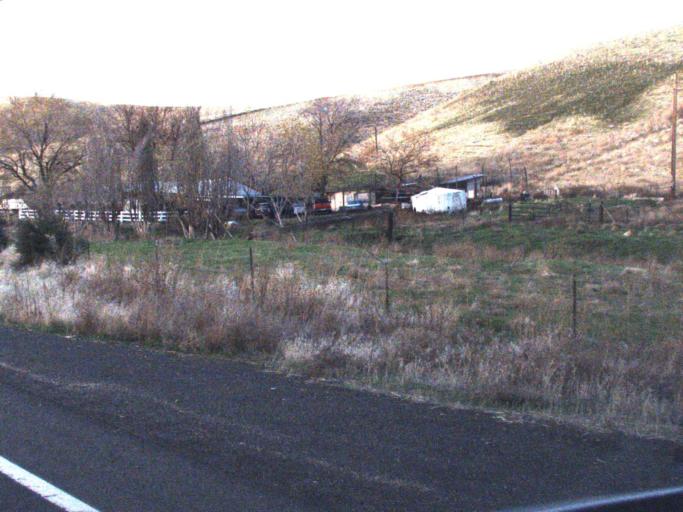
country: US
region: Washington
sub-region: Garfield County
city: Pomeroy
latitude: 46.6409
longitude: -117.8107
